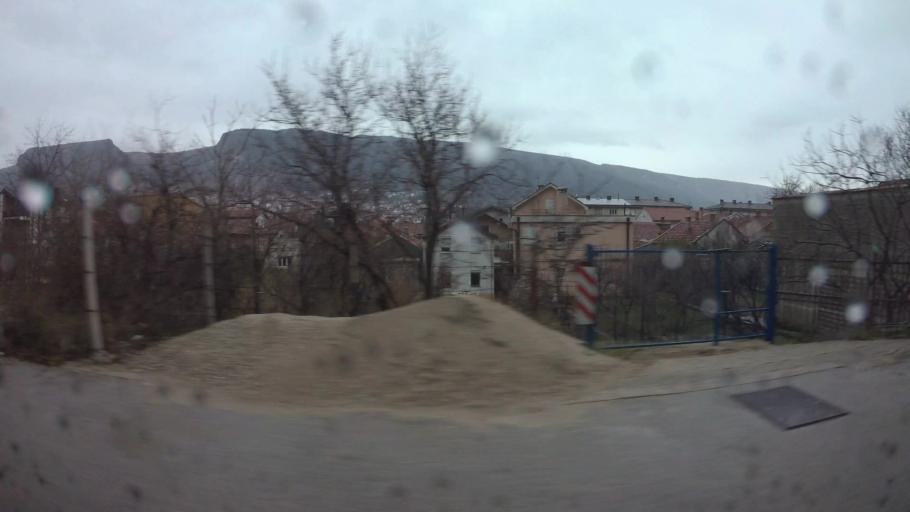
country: BA
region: Federation of Bosnia and Herzegovina
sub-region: Hercegovacko-Bosanski Kanton
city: Mostar
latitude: 43.3295
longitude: 17.8155
